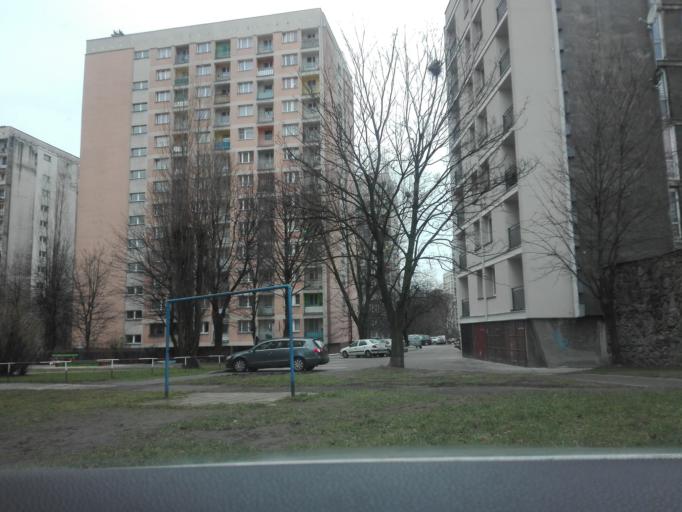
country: PL
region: Silesian Voivodeship
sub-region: Katowice
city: Katowice
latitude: 50.2686
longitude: 19.0268
